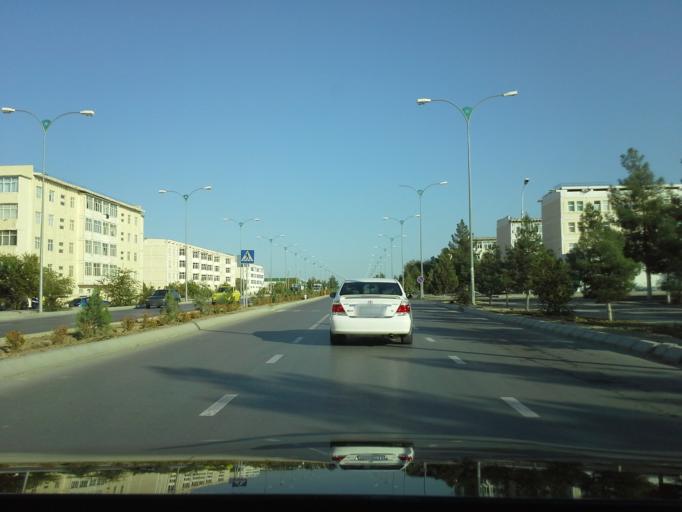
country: TM
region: Ahal
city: Abadan
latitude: 38.0545
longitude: 58.1525
